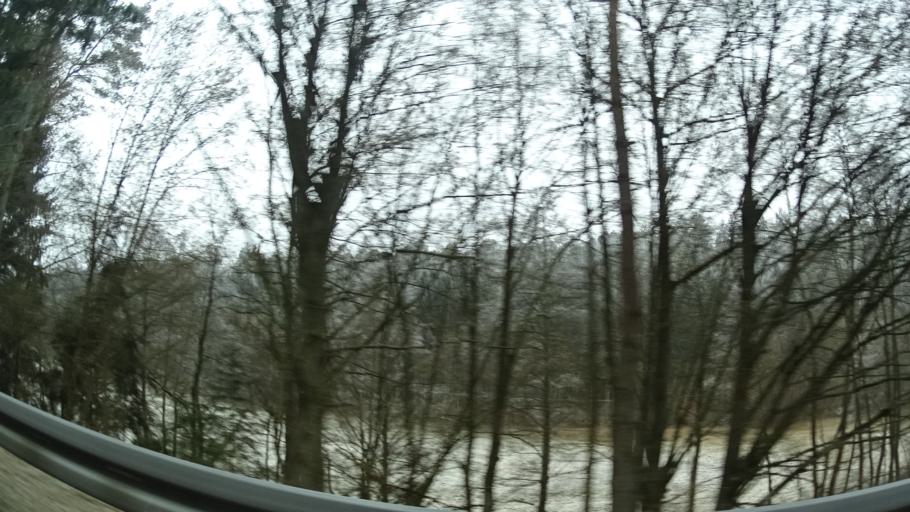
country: DE
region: Bavaria
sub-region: Regierungsbezirk Unterfranken
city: Obersinn
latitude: 50.2424
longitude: 9.5815
